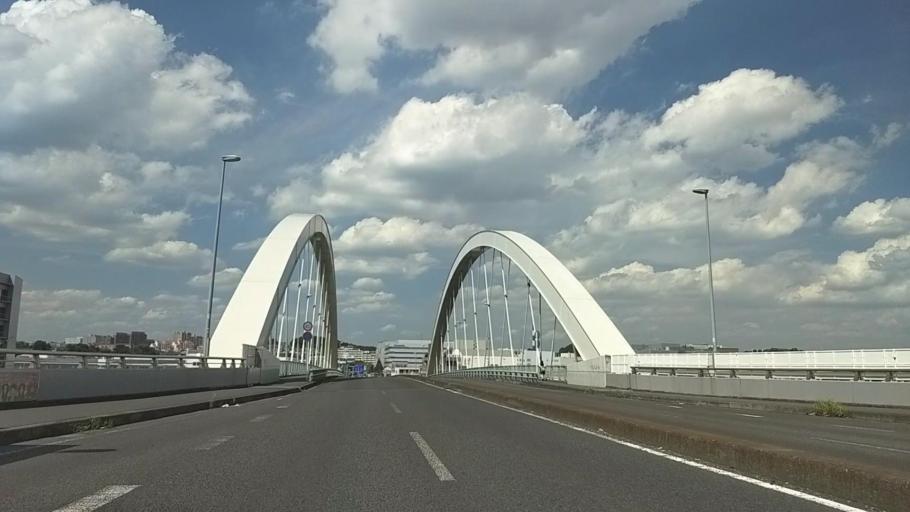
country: JP
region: Kanagawa
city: Yokohama
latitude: 35.5111
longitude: 139.5645
